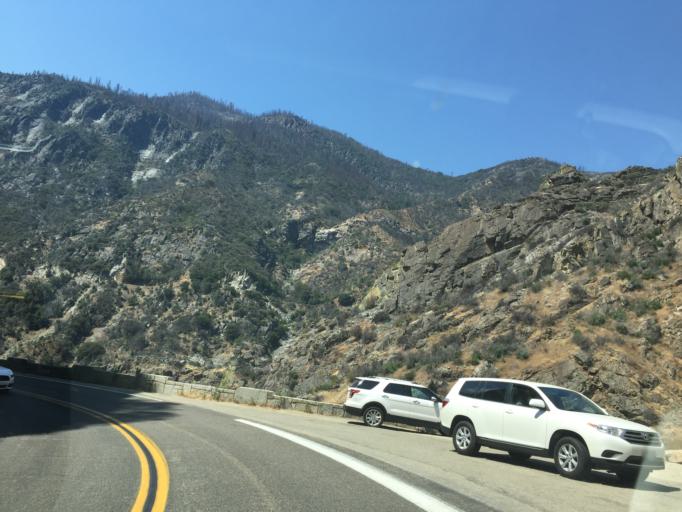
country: US
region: California
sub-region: Tulare County
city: Three Rivers
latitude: 36.8226
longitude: -118.8352
